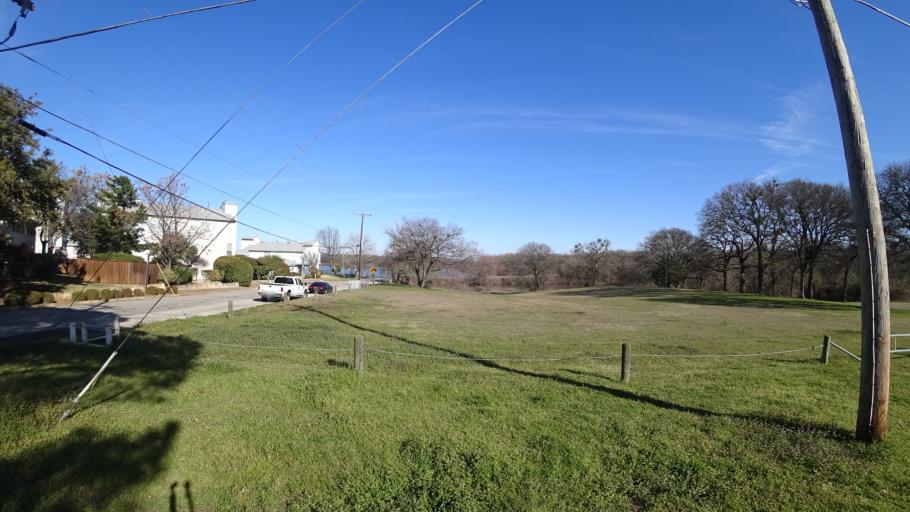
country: US
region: Texas
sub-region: Denton County
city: Highland Village
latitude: 33.0809
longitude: -97.0171
